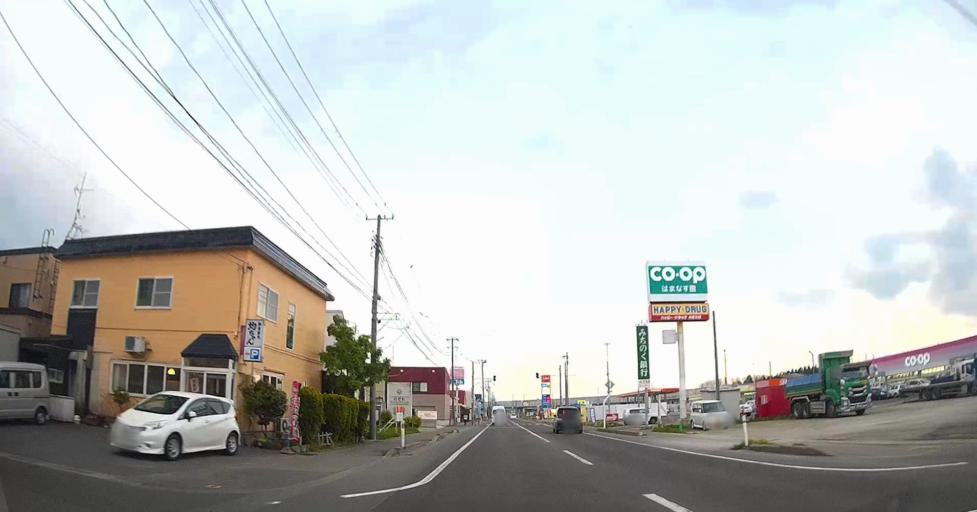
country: JP
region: Aomori
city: Aomori Shi
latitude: 40.8571
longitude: 140.6813
